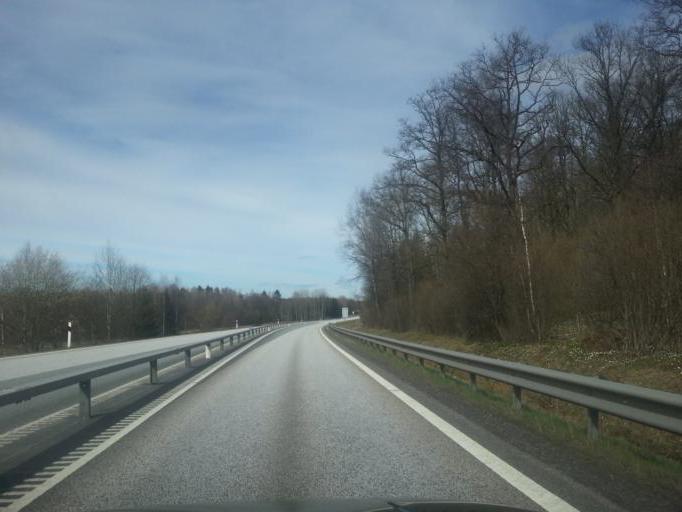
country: SE
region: Joenkoeping
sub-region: Jonkopings Kommun
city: Bankeryd
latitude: 57.8069
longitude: 14.0969
